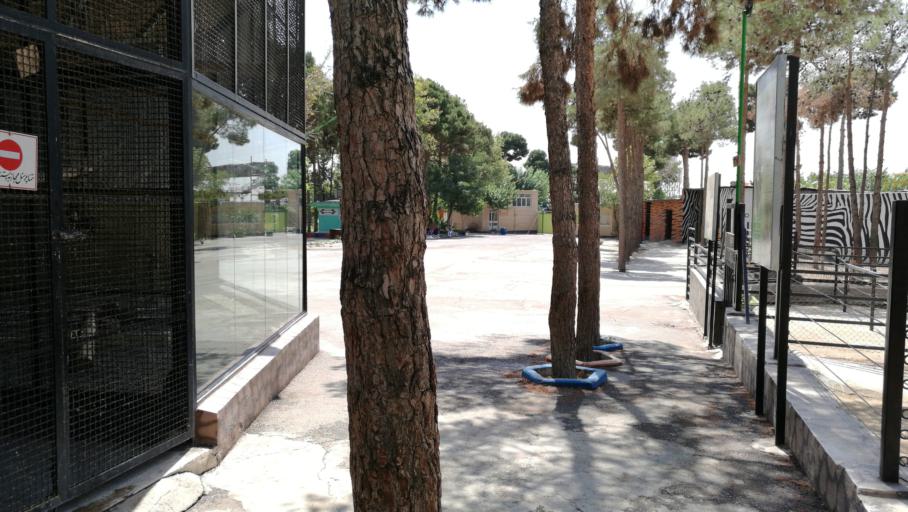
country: IR
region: Tehran
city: Tehran
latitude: 35.7183
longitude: 51.2928
